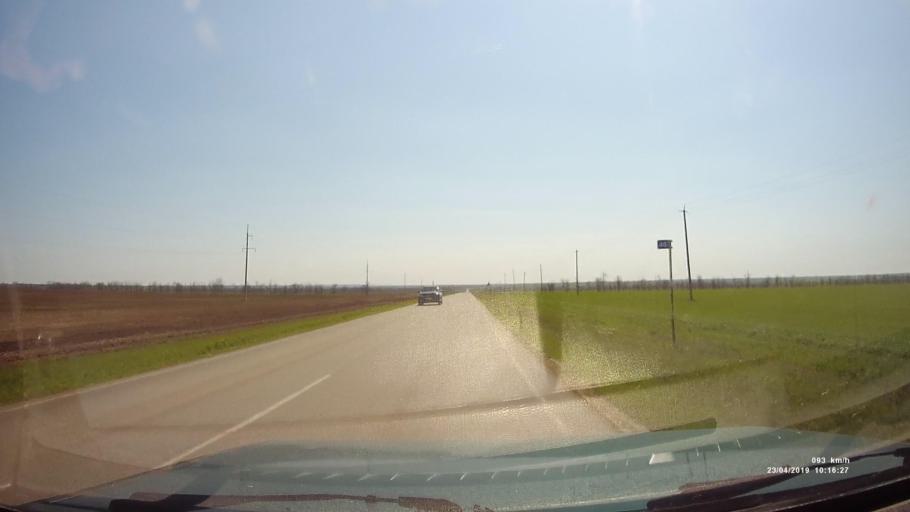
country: RU
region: Rostov
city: Sovetskoye
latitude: 46.6584
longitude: 42.3959
